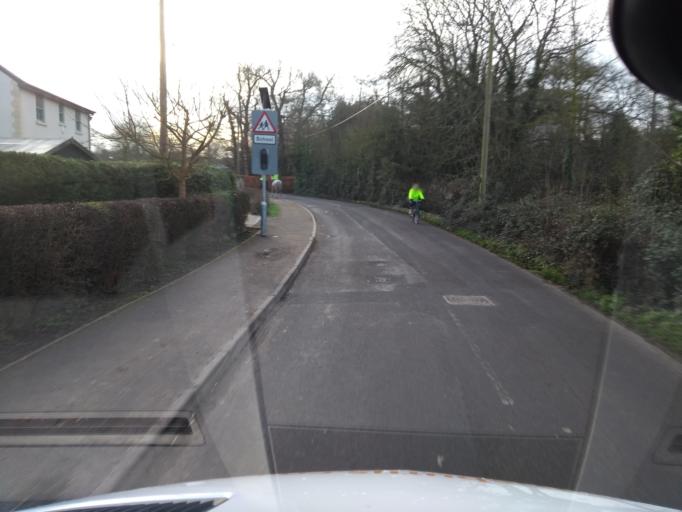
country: GB
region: England
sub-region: North Somerset
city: Bleadon
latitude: 51.2850
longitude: -2.9554
